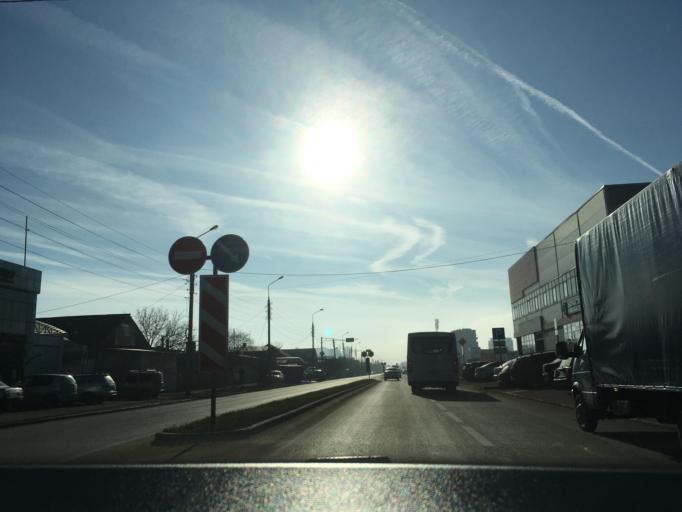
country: RU
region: Krasnodarskiy
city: Krasnodar
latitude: 45.1191
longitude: 39.0115
